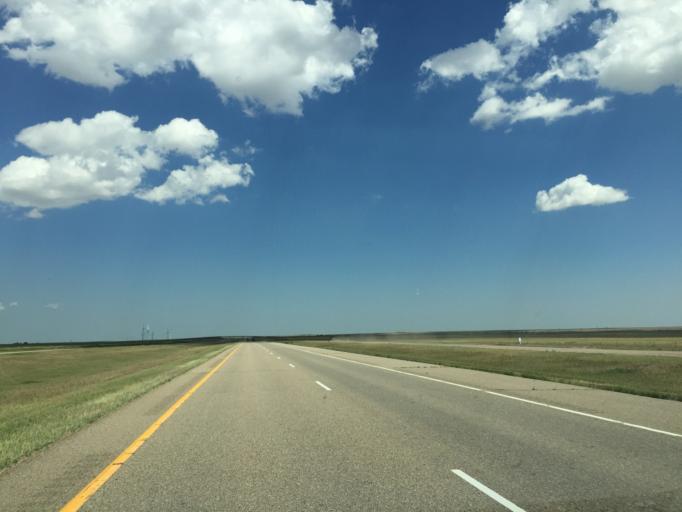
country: US
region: Colorado
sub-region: Lincoln County
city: Hugo
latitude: 39.2772
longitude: -103.4623
